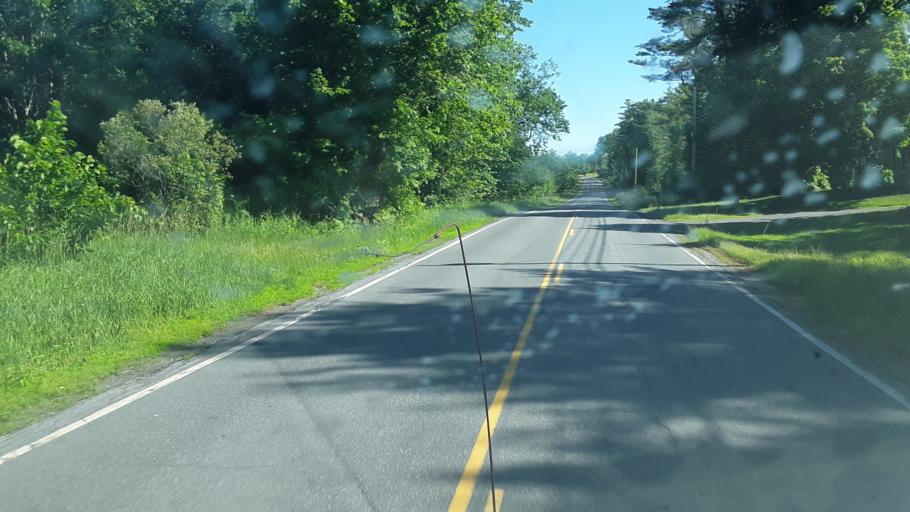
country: US
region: New Hampshire
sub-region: Grafton County
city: Haverhill
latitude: 44.0111
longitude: -72.0696
